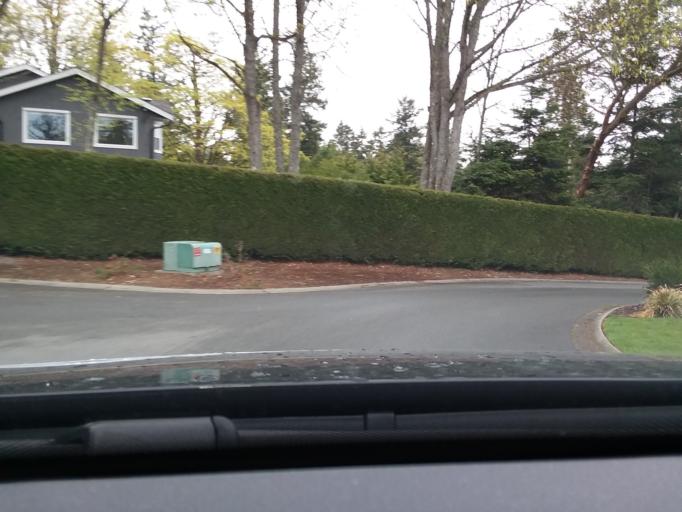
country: CA
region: British Columbia
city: Victoria
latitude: 48.5221
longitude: -123.3803
